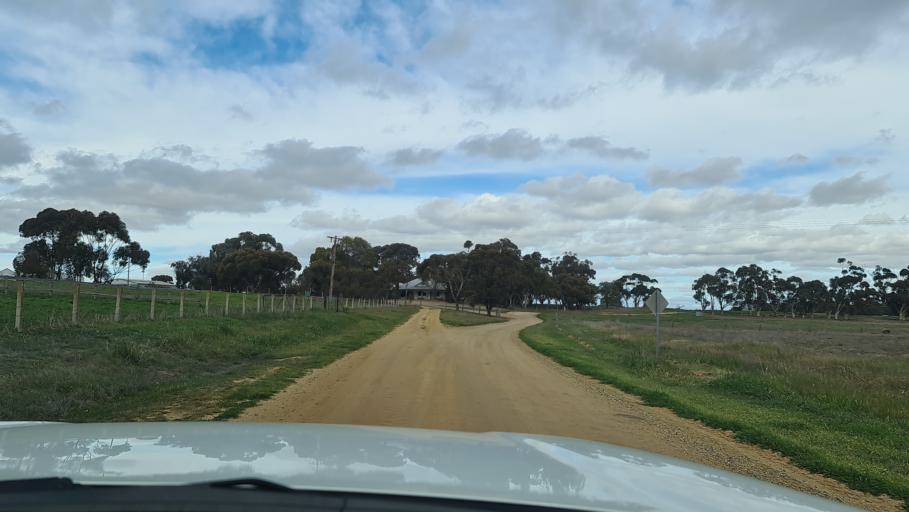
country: AU
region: Victoria
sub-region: Horsham
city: Horsham
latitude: -36.6230
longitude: 142.4208
